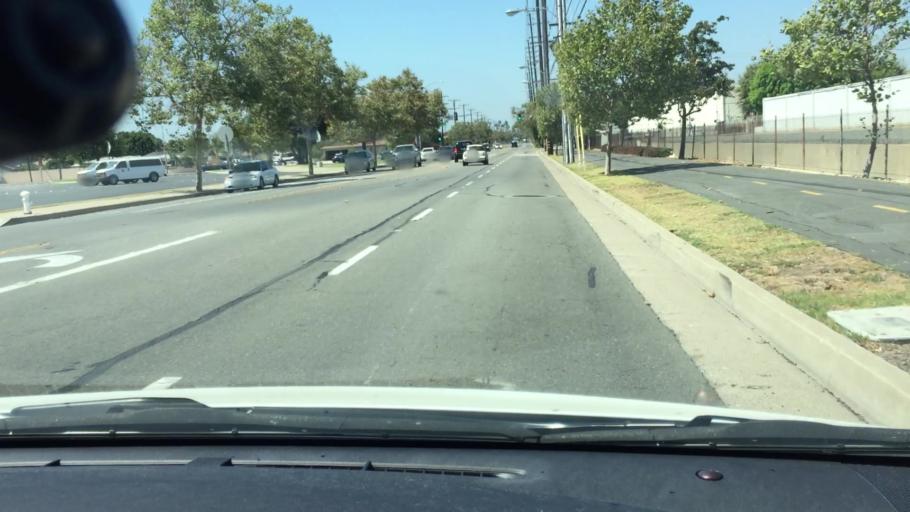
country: US
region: California
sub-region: Orange County
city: Santa Ana
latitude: 33.7082
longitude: -117.8768
